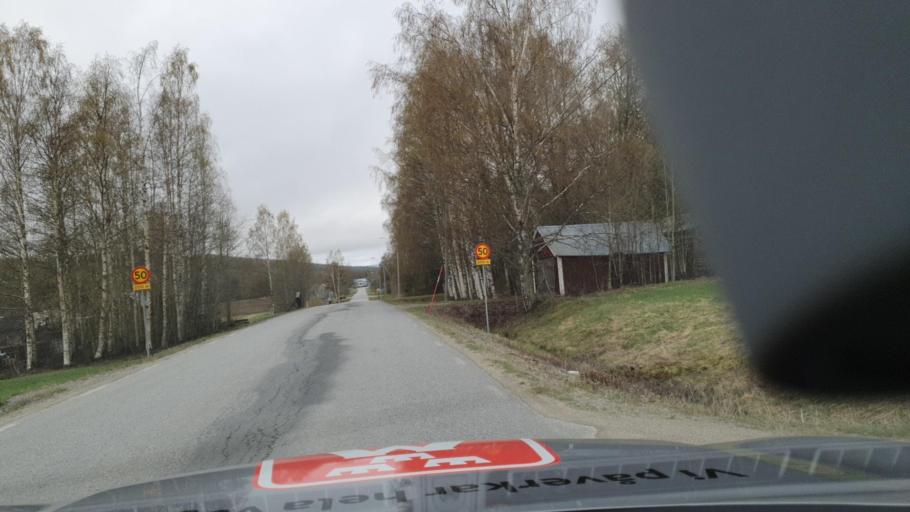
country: SE
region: Vaesternorrland
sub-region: OErnskoeldsviks Kommun
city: Husum
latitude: 63.5726
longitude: 19.0360
